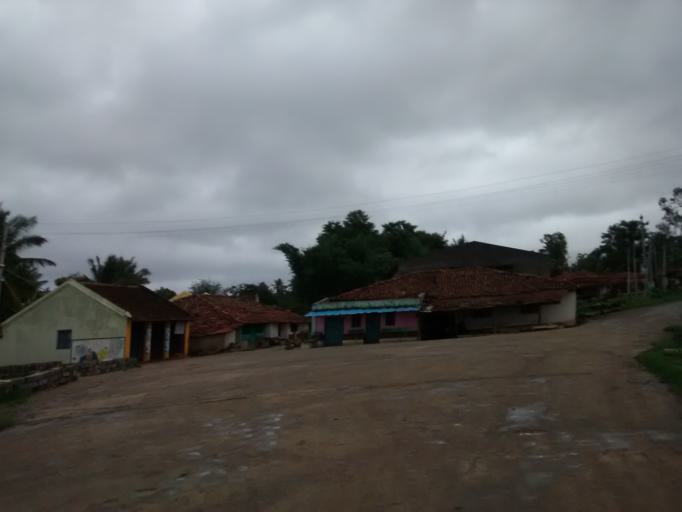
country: IN
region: Karnataka
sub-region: Hassan
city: Hassan
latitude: 12.9289
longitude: 76.1867
